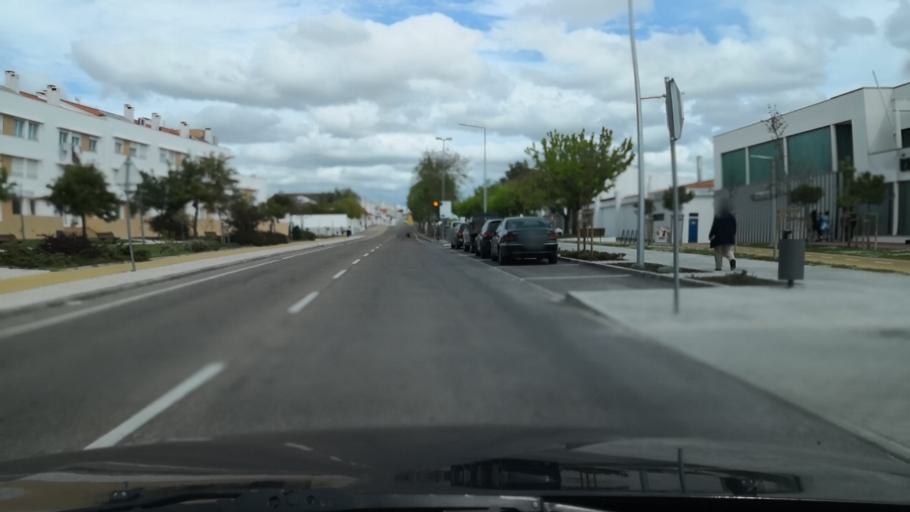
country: PT
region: Evora
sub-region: Vendas Novas
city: Vendas Novas
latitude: 38.6741
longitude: -8.4632
